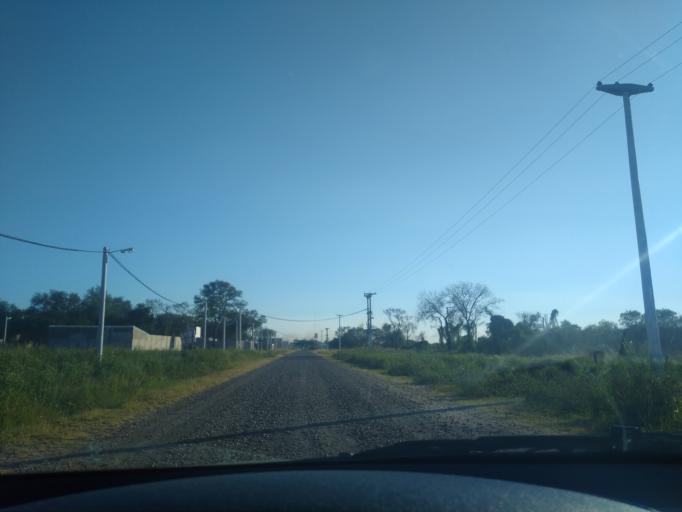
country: AR
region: Chaco
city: Resistencia
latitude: -27.4097
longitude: -58.9545
